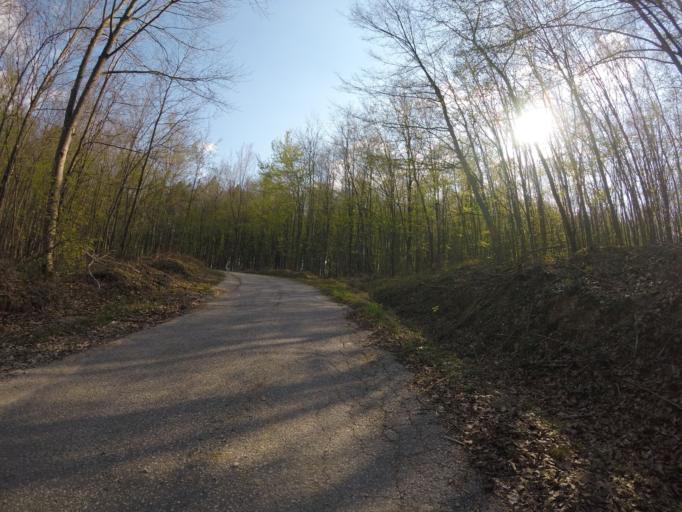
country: HR
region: Sisacko-Moslavacka
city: Glina
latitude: 45.5013
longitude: 16.0085
